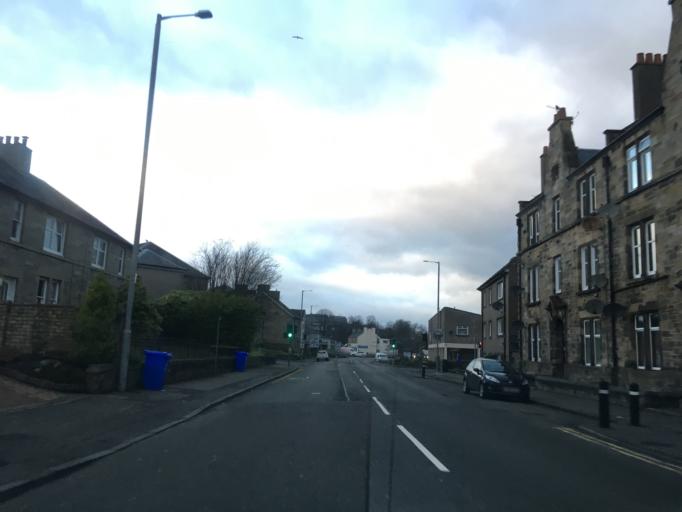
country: GB
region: Scotland
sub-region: Stirling
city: Stirling
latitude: 56.0997
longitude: -3.9343
